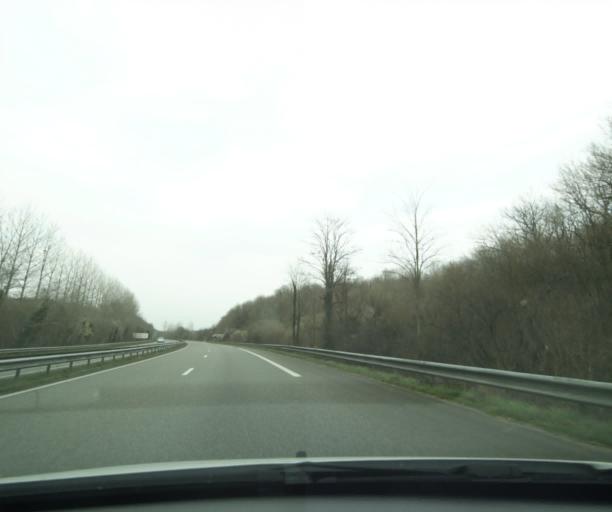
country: FR
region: Aquitaine
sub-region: Departement des Pyrenees-Atlantiques
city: Briscous
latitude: 43.4480
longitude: -1.3157
